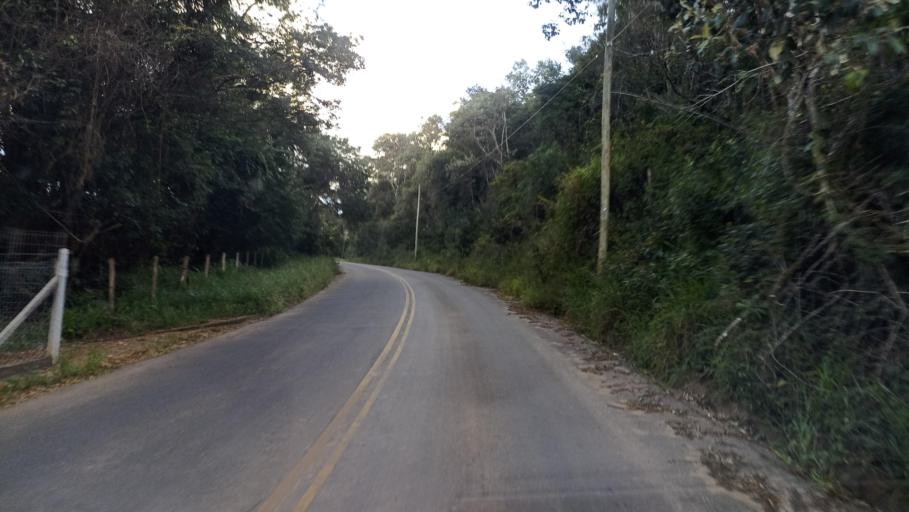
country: BR
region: Minas Gerais
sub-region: Ouro Preto
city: Ouro Preto
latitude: -20.3136
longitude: -43.6154
